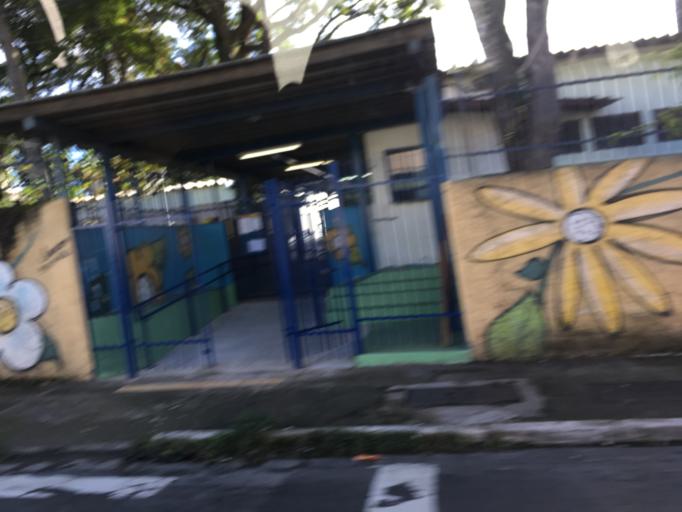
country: BR
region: Sao Paulo
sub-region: Osasco
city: Osasco
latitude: -23.5202
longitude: -46.7419
